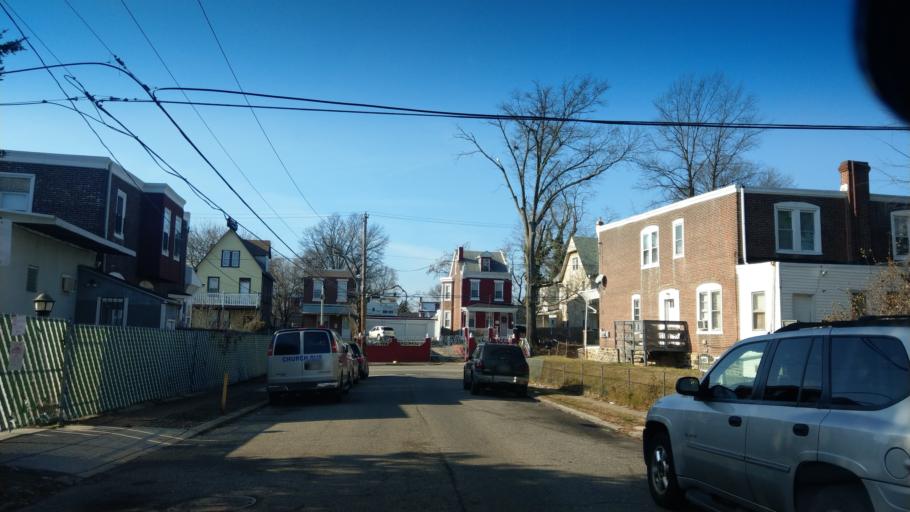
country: US
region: Pennsylvania
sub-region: Montgomery County
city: Rockledge
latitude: 40.0348
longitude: -75.1233
